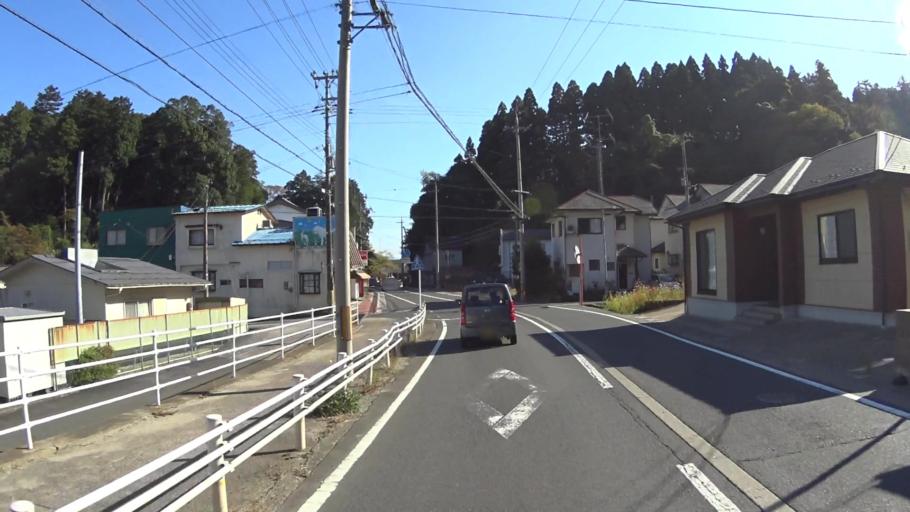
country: JP
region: Kyoto
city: Miyazu
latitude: 35.6318
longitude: 135.0547
